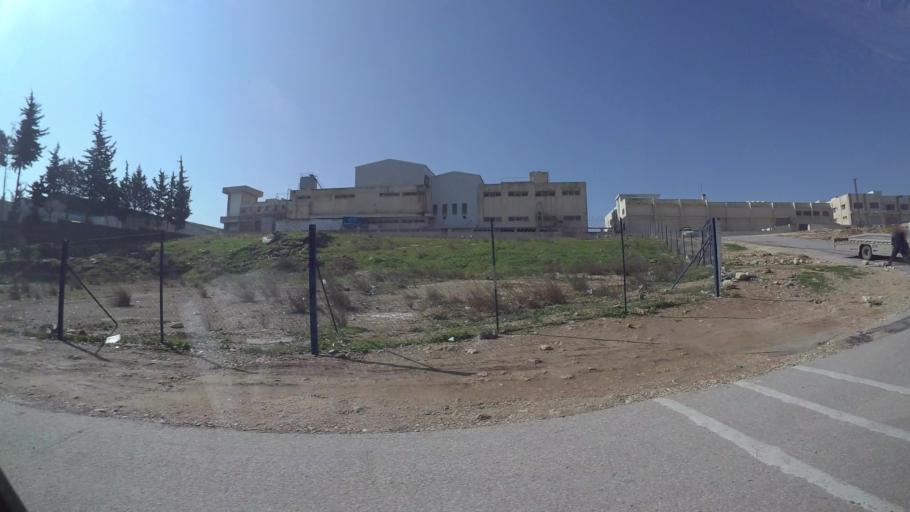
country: JO
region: Amman
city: Al Bunayyat ash Shamaliyah
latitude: 31.9179
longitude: 35.9009
